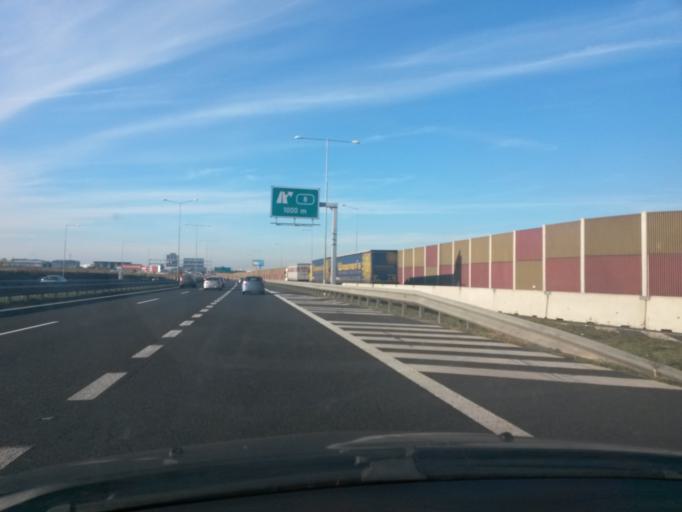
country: CZ
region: Central Bohemia
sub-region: Okres Praha-Vychod
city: Ricany
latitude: 49.9842
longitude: 14.6023
